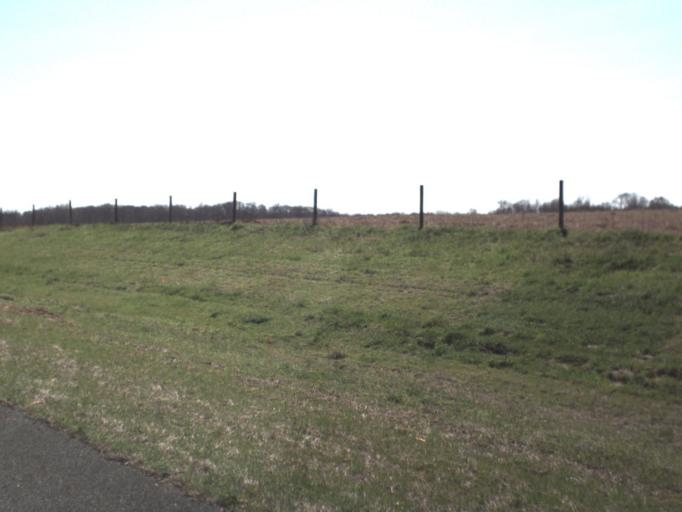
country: US
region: Florida
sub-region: Jackson County
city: Marianna
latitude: 30.8636
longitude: -85.3567
